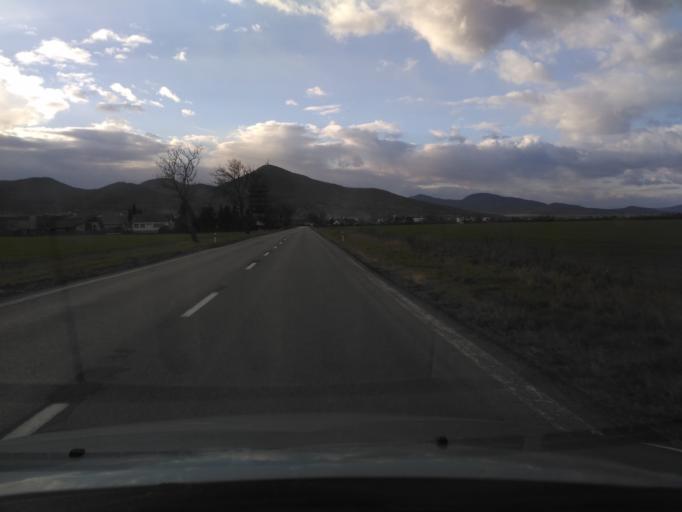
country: HU
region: Borsod-Abauj-Zemplen
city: Satoraljaujhely
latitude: 48.3973
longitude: 21.6880
